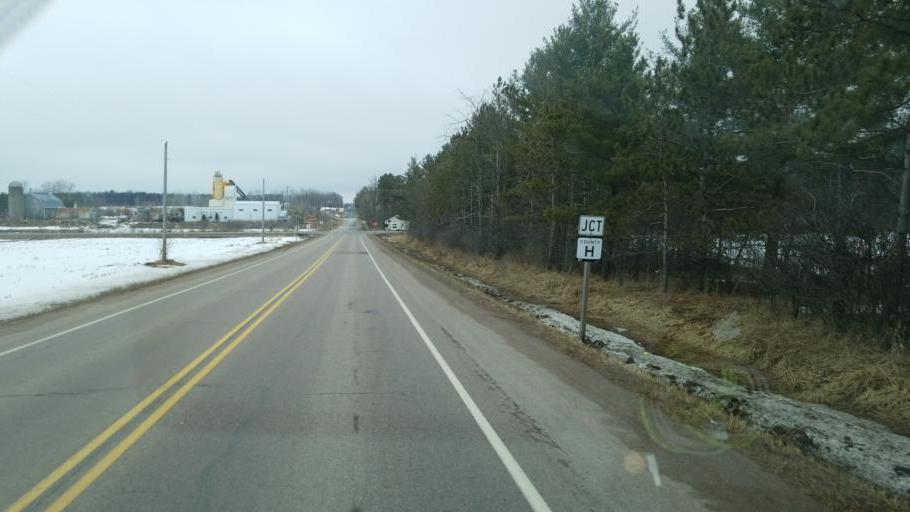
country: US
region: Wisconsin
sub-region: Wood County
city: Marshfield
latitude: 44.6542
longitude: -90.2184
